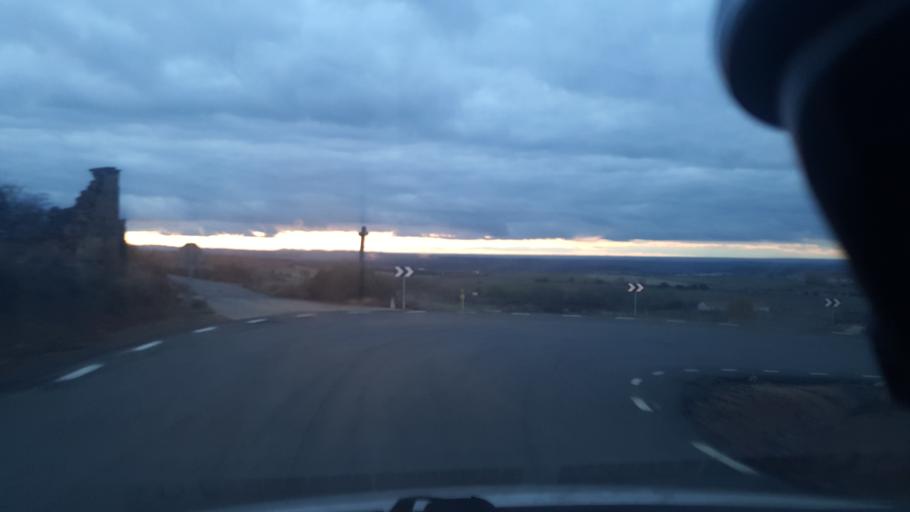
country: ES
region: Castille and Leon
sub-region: Provincia de Avila
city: Ojos-Albos
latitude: 40.7394
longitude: -4.4732
